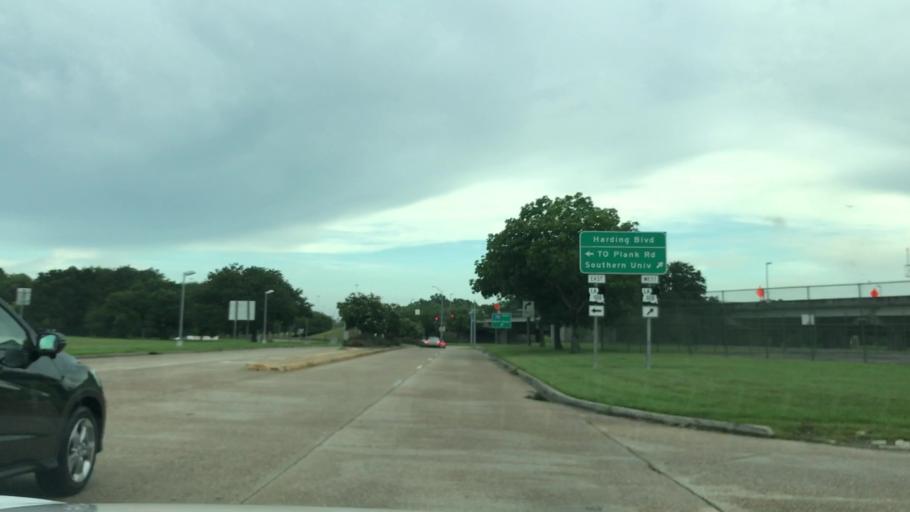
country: US
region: Louisiana
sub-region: East Baton Rouge Parish
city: Brownsfield
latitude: 30.5228
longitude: -91.1611
